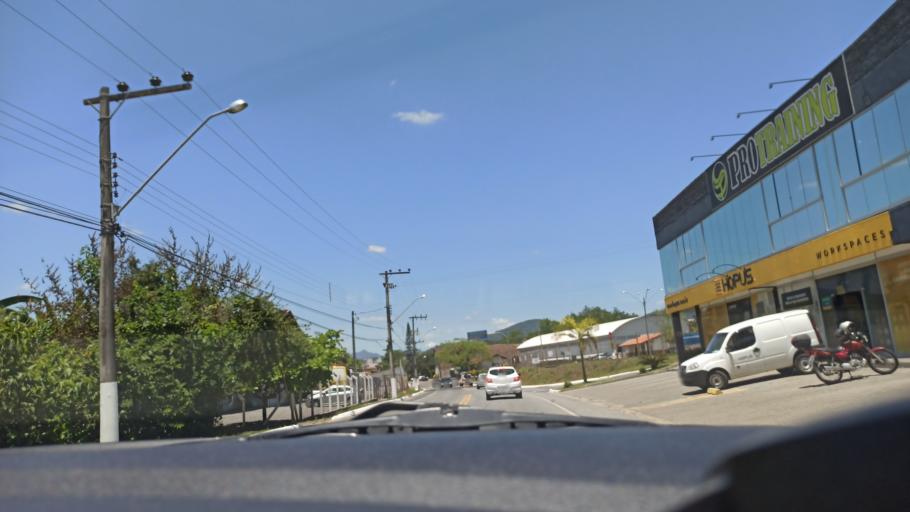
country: BR
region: Santa Catarina
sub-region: Indaial
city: Indaial
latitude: -26.8892
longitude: -49.2385
